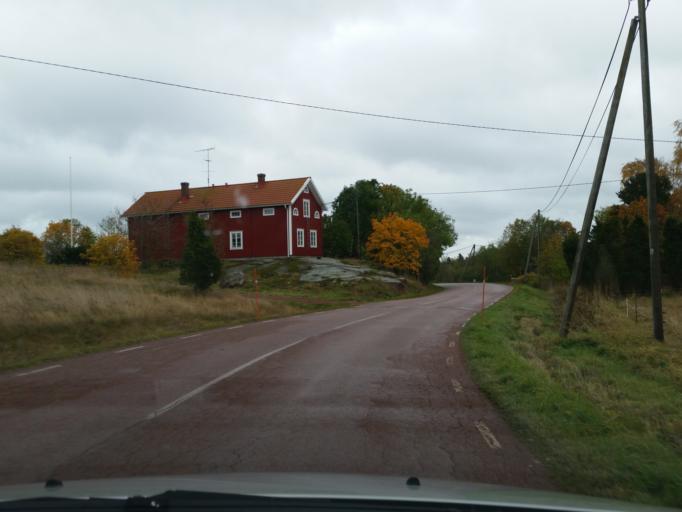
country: AX
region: Alands landsbygd
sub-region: Lumparland
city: Lumparland
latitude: 60.1224
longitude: 20.2433
